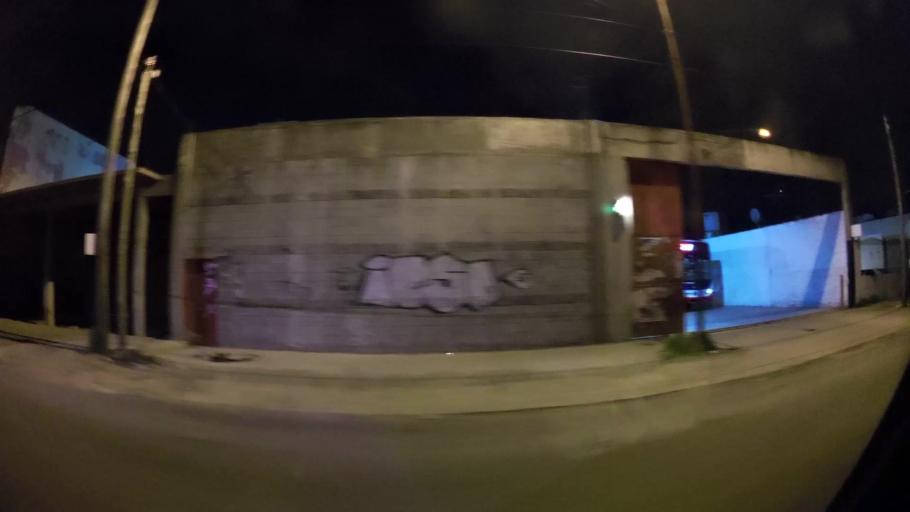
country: AR
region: Buenos Aires
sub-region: Partido de Lanus
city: Lanus
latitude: -34.7202
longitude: -58.3413
